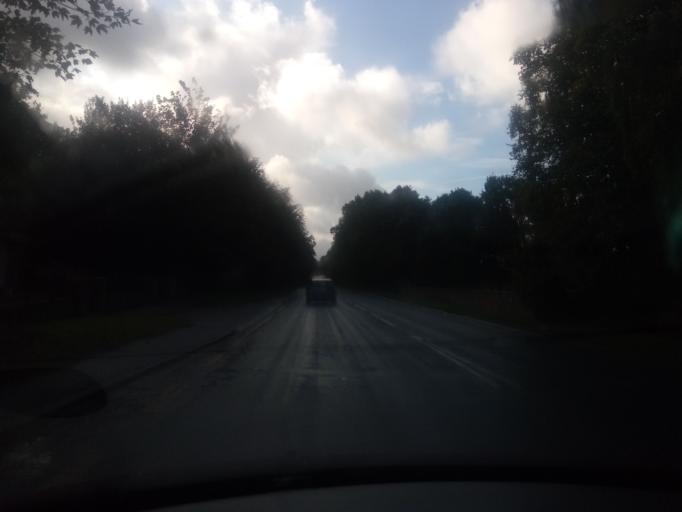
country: GB
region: England
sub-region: Cumbria
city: Carlisle
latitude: 54.9378
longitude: -2.9448
